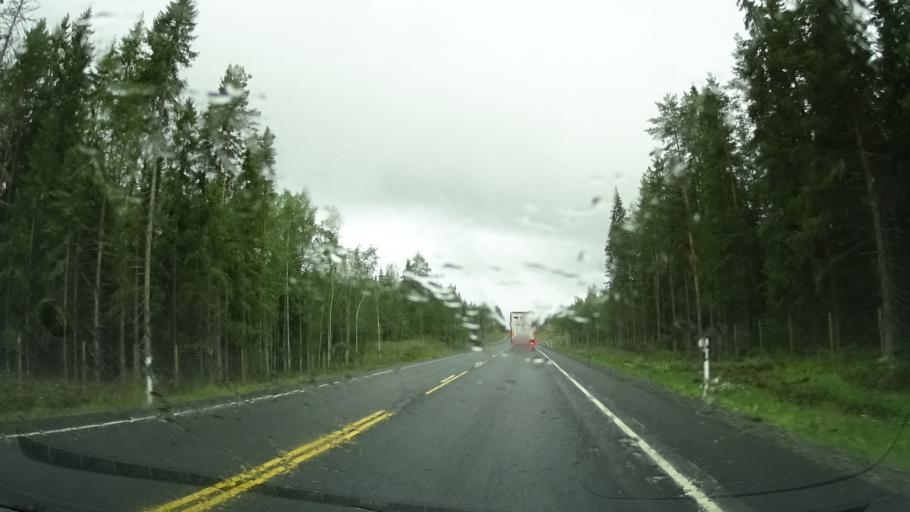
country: FI
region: Haeme
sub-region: Forssa
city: Tammela
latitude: 60.7311
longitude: 23.7477
